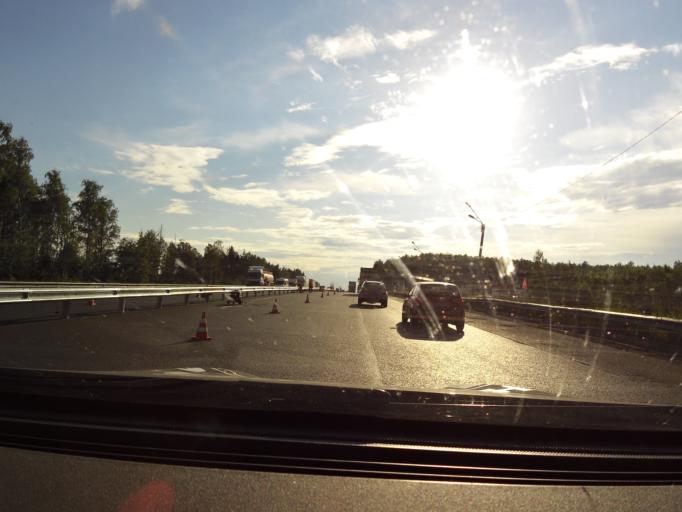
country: RU
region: Vladimir
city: Melekhovo
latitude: 56.2113
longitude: 41.3049
